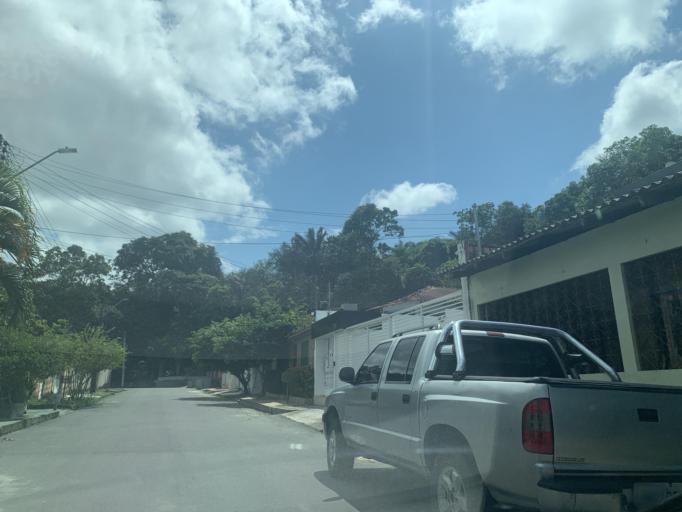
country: BR
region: Amazonas
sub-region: Manaus
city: Manaus
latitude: -3.1016
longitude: -59.9638
